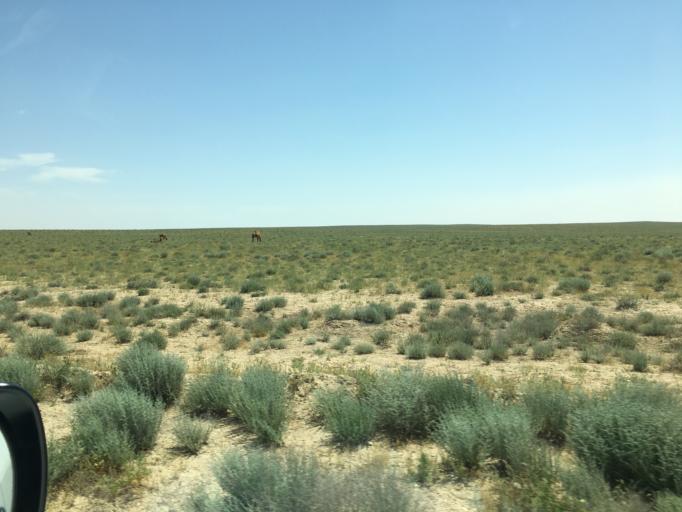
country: TM
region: Balkan
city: Turkmenbasy
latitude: 40.1277
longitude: 53.4305
